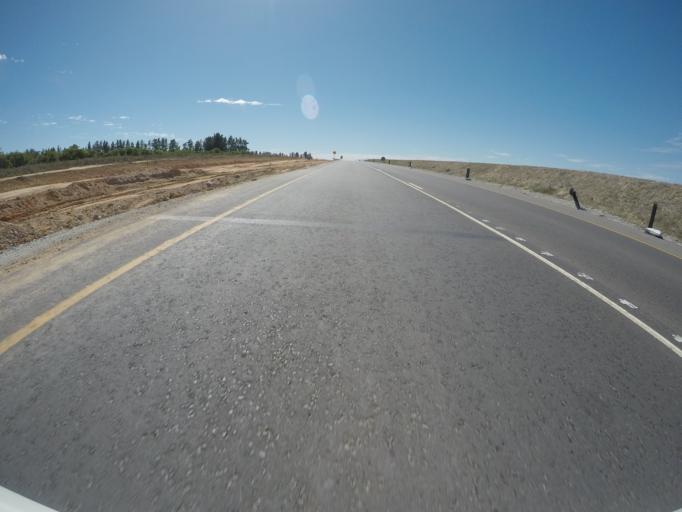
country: ZA
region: Western Cape
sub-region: West Coast District Municipality
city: Malmesbury
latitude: -33.5035
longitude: 18.6623
